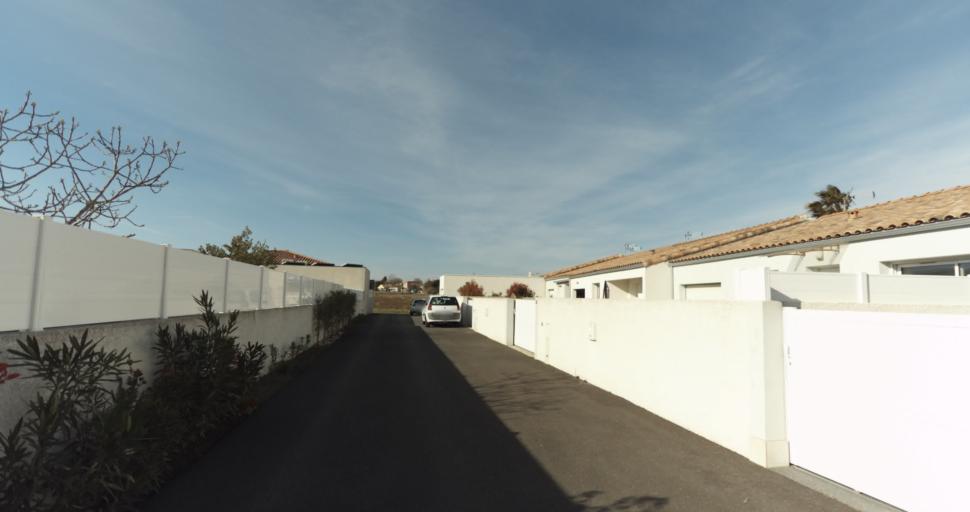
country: FR
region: Languedoc-Roussillon
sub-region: Departement de l'Herault
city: Marseillan
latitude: 43.3611
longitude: 3.5226
